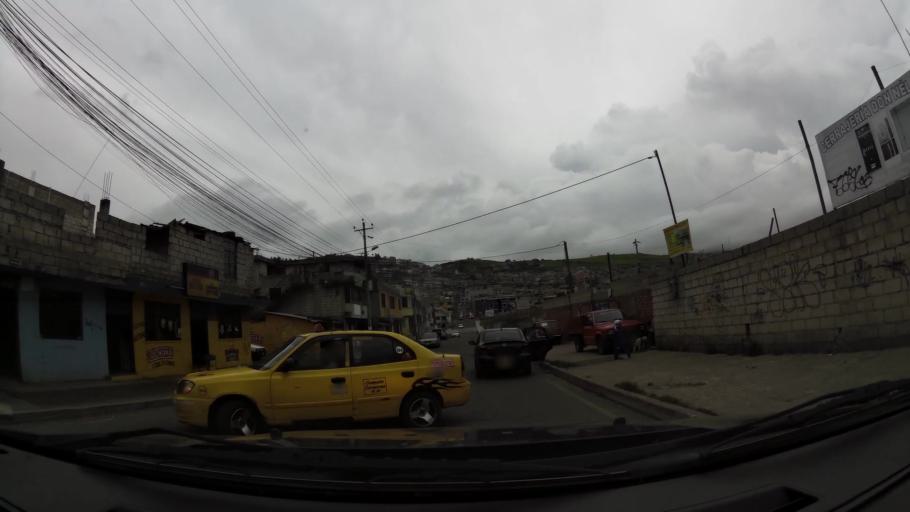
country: EC
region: Pichincha
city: Sangolqui
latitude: -0.3188
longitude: -78.5375
